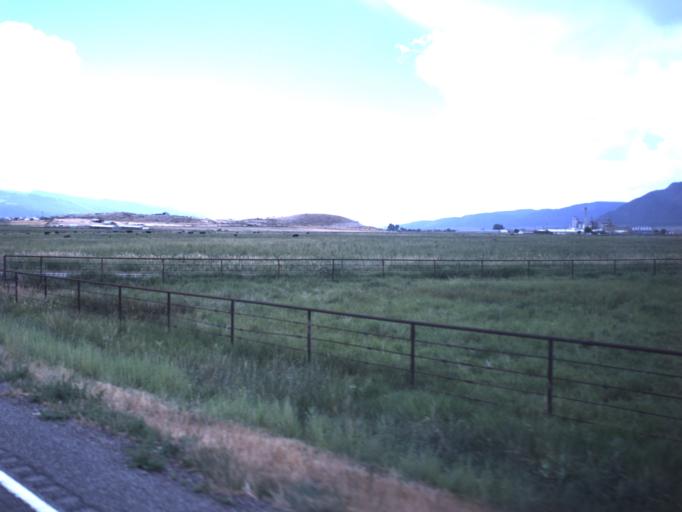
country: US
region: Utah
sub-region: Sanpete County
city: Moroni
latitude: 39.5134
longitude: -111.5714
